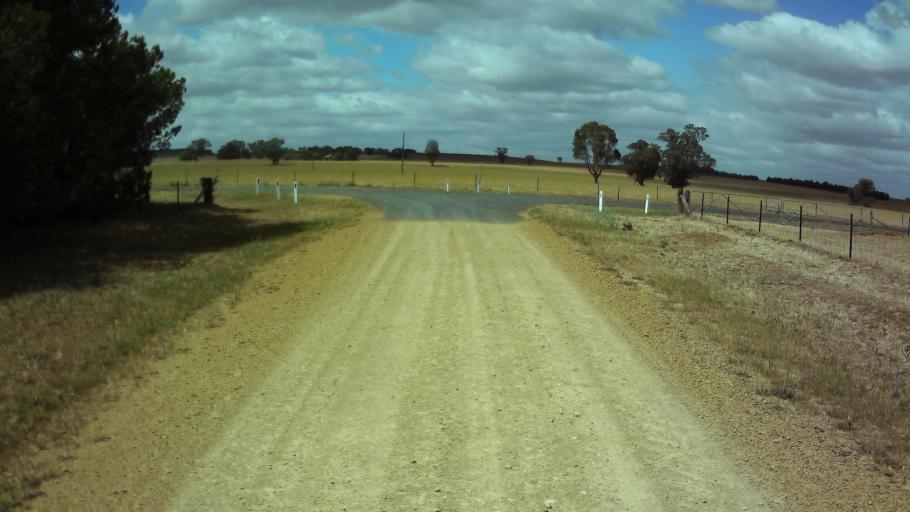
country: AU
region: New South Wales
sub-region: Weddin
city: Grenfell
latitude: -34.0669
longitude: 148.3290
